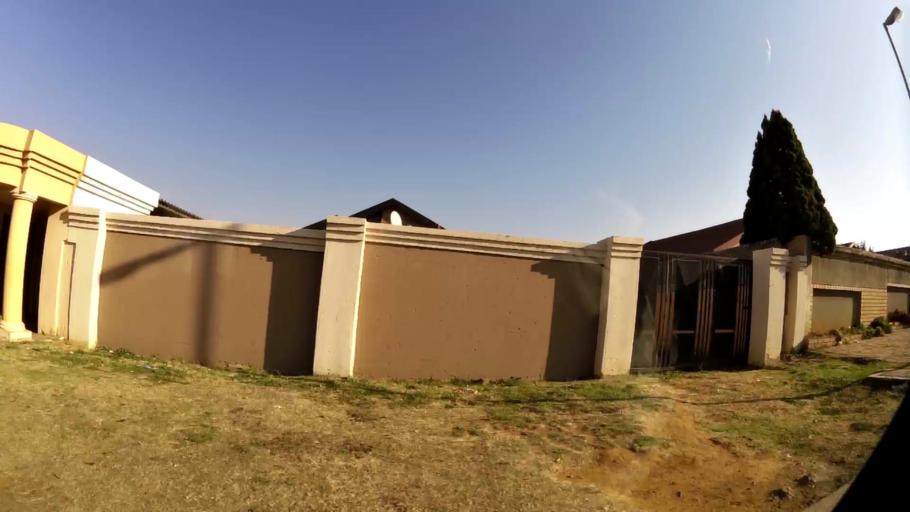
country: ZA
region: Gauteng
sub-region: City of Johannesburg Metropolitan Municipality
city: Soweto
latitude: -26.2951
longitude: 27.9602
